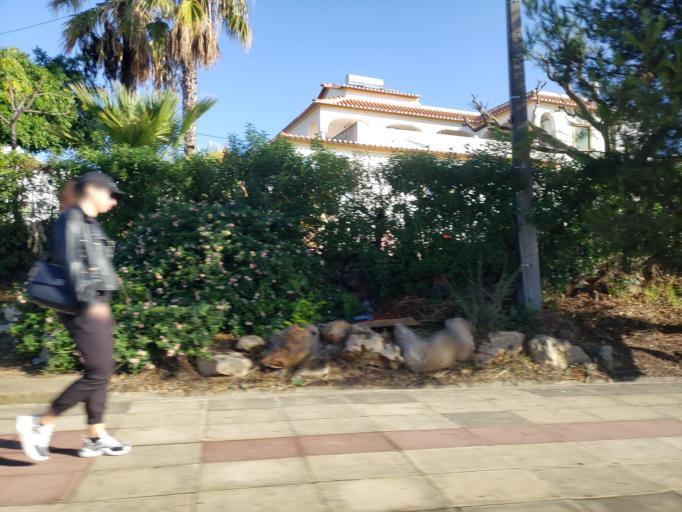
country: PT
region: Faro
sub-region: Portimao
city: Portimao
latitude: 37.1487
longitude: -8.5480
